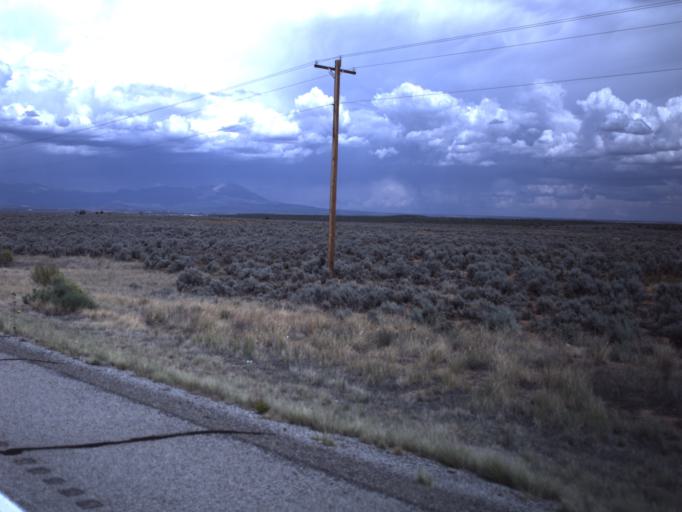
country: US
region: Utah
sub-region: San Juan County
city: Blanding
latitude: 37.4988
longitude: -109.4844
